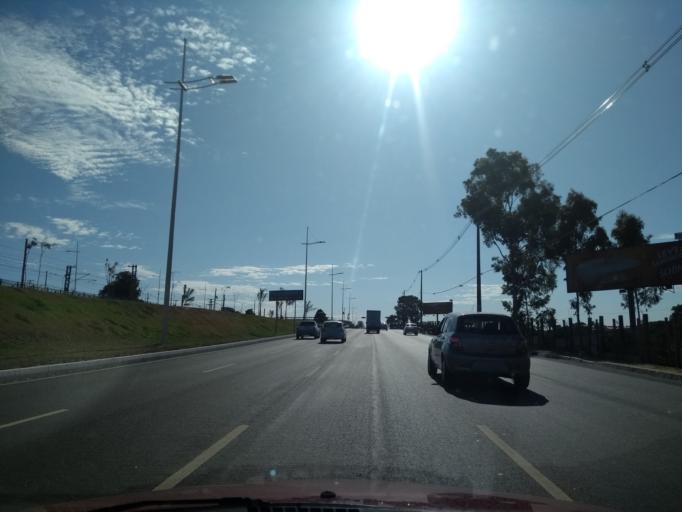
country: BR
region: Bahia
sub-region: Lauro De Freitas
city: Lauro de Freitas
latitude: -12.9239
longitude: -38.3735
